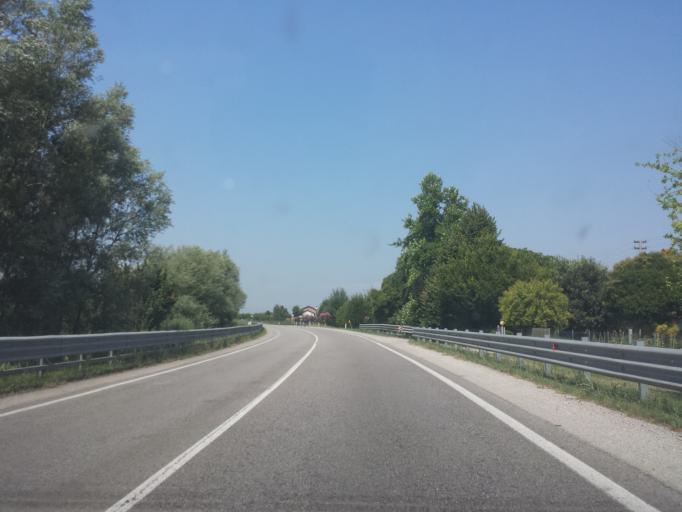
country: IT
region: Veneto
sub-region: Provincia di Venezia
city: Passarella
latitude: 45.5710
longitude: 12.5631
